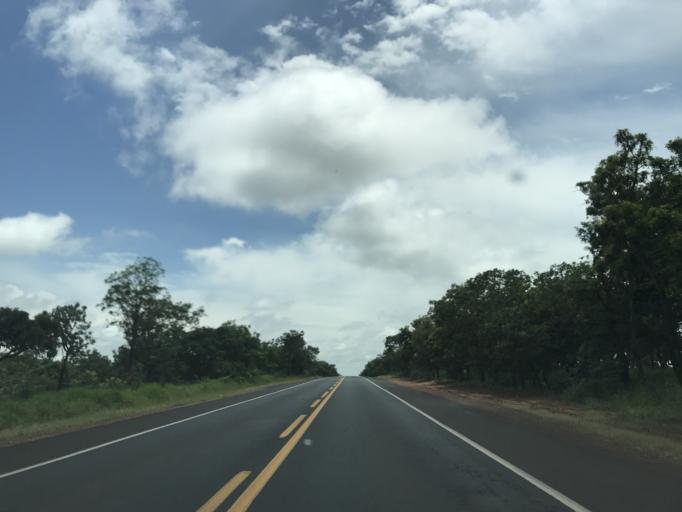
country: BR
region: Minas Gerais
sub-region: Prata
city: Prata
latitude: -19.6291
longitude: -48.9010
